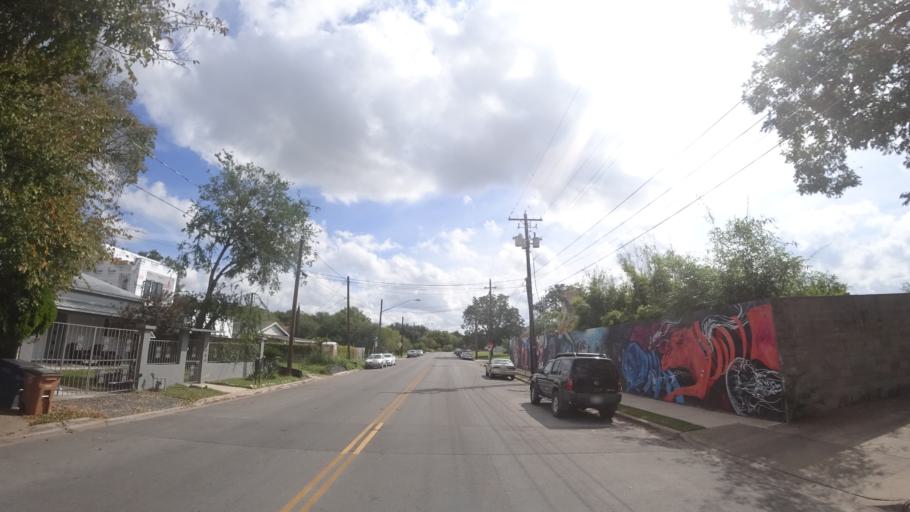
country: US
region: Texas
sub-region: Travis County
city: Austin
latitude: 30.2534
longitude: -97.7110
